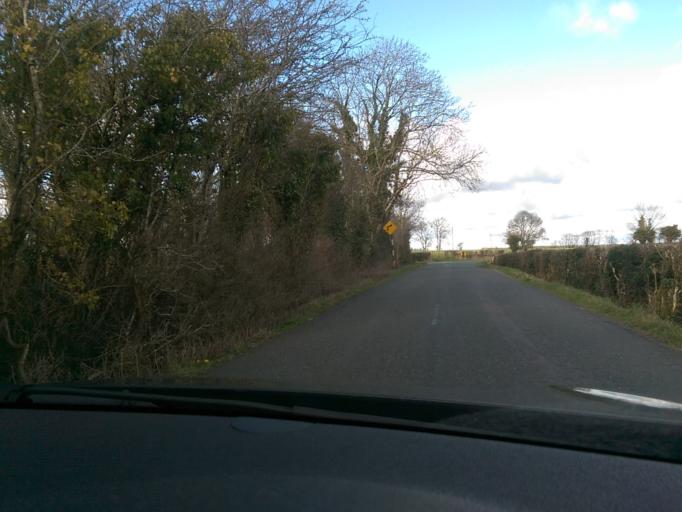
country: IE
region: Connaught
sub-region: County Galway
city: Athenry
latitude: 53.4631
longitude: -8.5465
